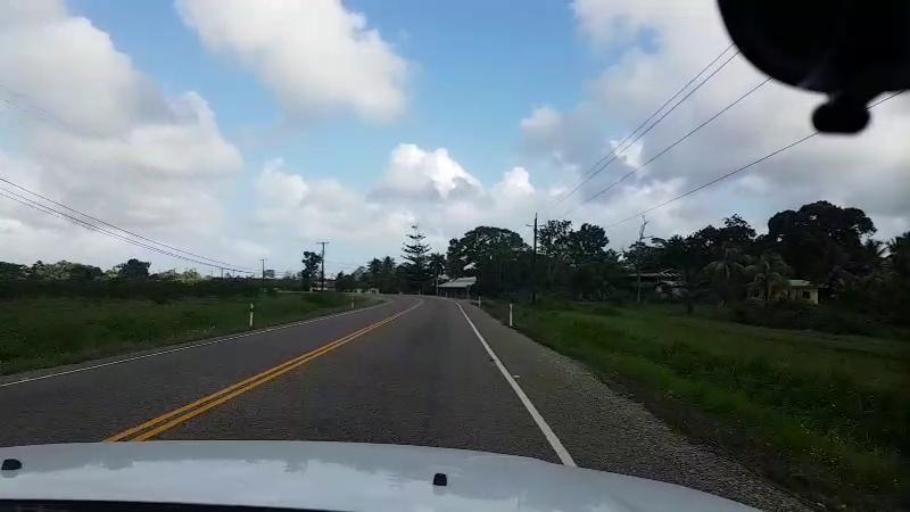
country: BZ
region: Stann Creek
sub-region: Dangriga
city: Dangriga
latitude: 16.9944
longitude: -88.3634
